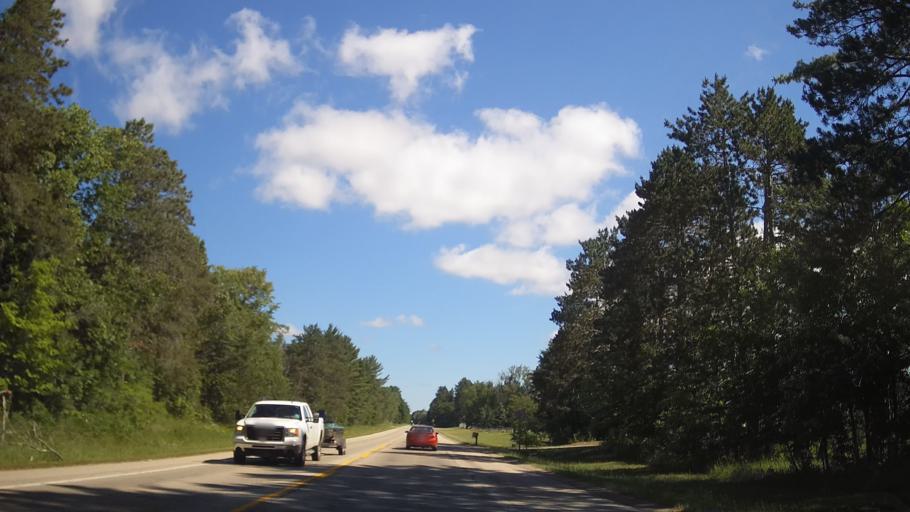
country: US
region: Michigan
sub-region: Cheboygan County
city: Indian River
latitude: 45.4604
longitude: -84.7828
